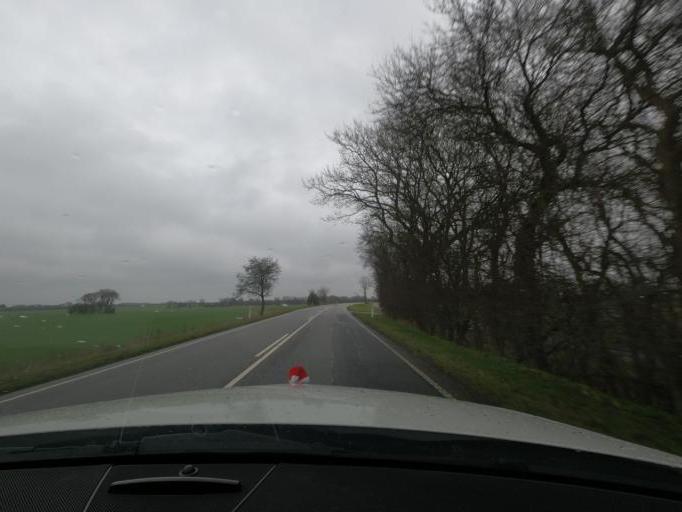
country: DK
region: South Denmark
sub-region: Haderslev Kommune
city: Starup
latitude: 55.2551
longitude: 9.6199
